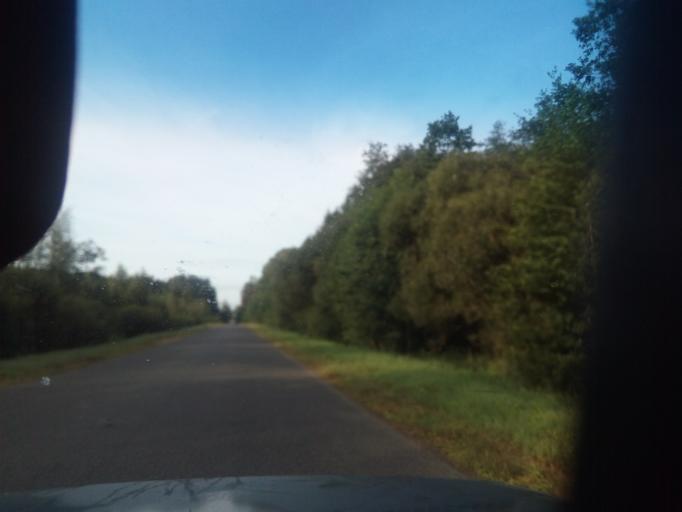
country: BY
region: Vitebsk
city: Dzisna
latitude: 55.6463
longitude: 28.3200
